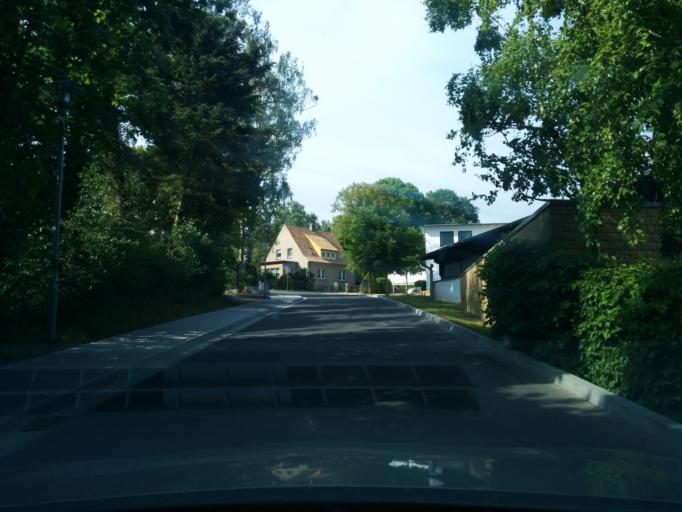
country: DE
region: Mecklenburg-Vorpommern
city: Ostseebad Zinnowitz
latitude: 54.0728
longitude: 13.9187
